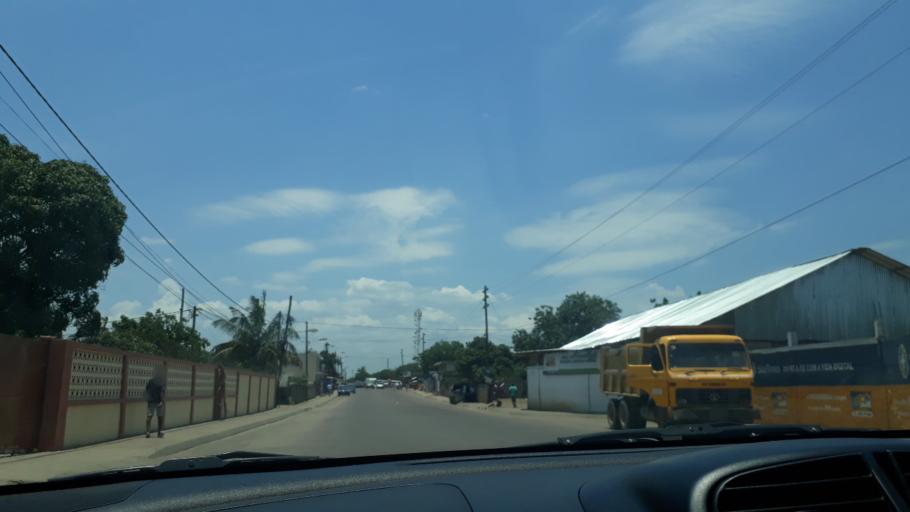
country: MZ
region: Maputo City
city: Maputo
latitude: -25.8812
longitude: 32.6051
